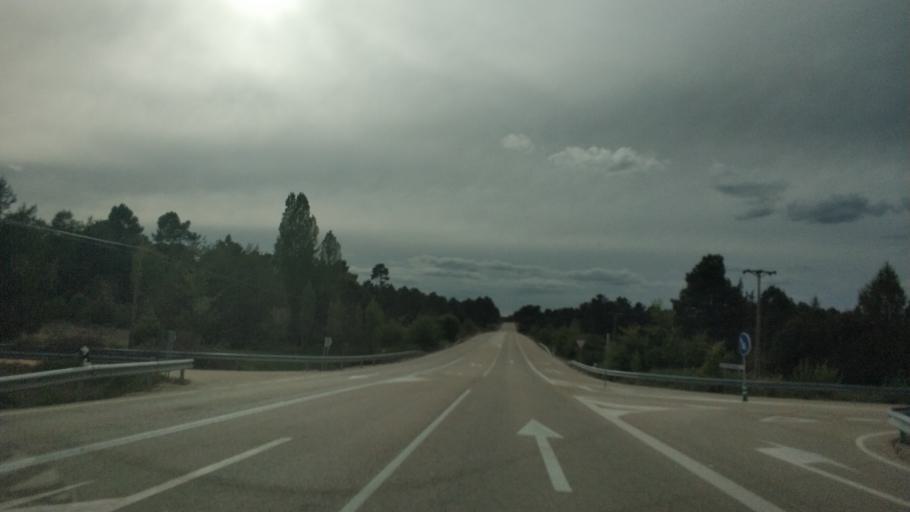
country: ES
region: Castille and Leon
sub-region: Provincia de Soria
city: Valdenebro
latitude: 41.5599
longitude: -2.9731
